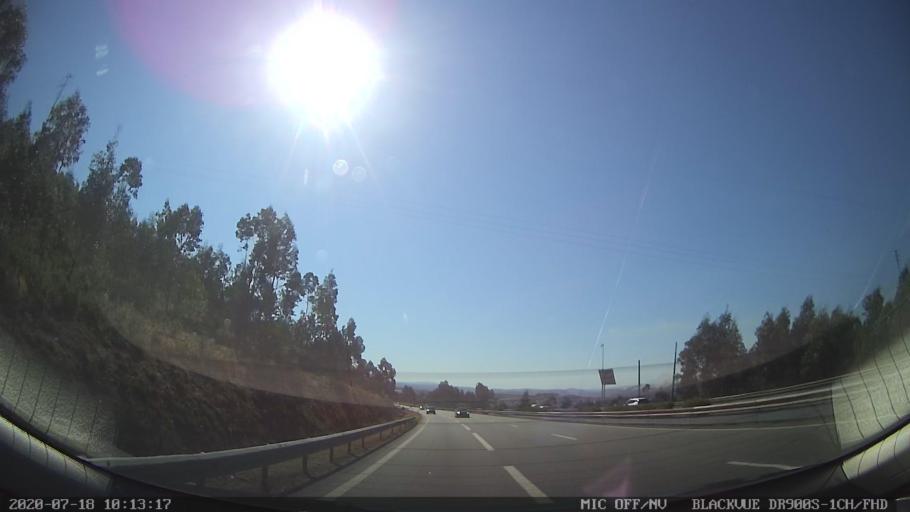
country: PT
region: Porto
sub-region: Valongo
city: Campo
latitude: 41.1894
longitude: -8.4784
